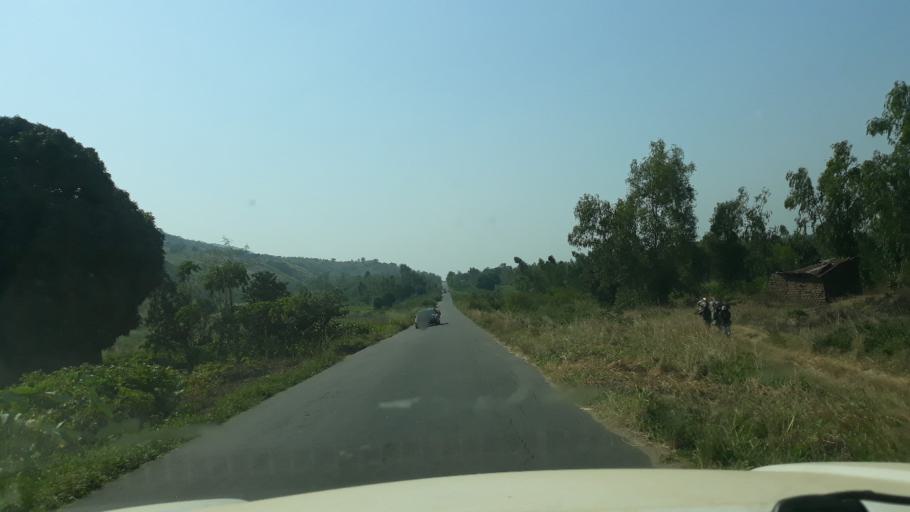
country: CD
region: South Kivu
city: Uvira
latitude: -3.2995
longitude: 29.1604
